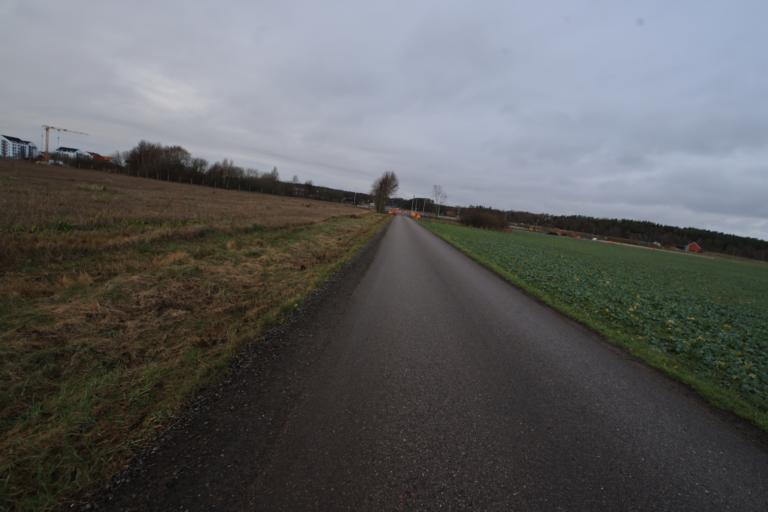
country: SE
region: Halland
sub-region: Varbergs Kommun
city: Traslovslage
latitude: 57.0875
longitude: 12.2919
